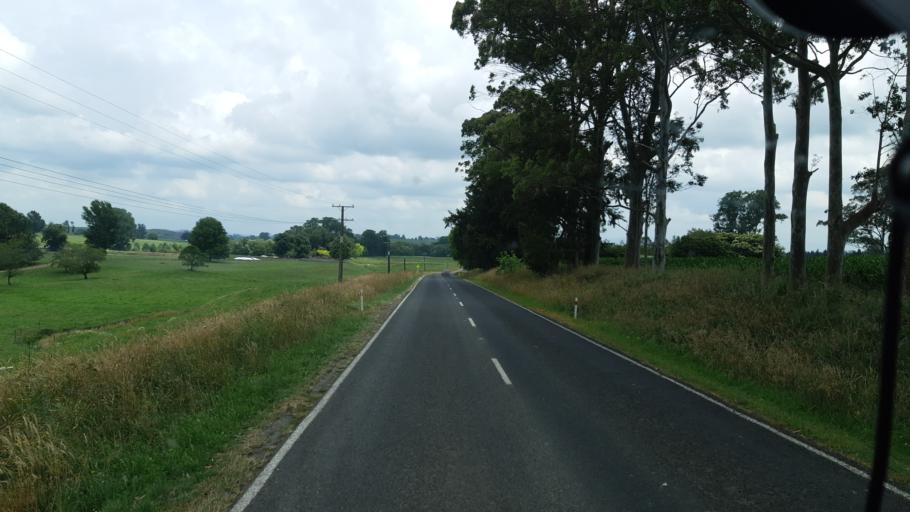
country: NZ
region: Waikato
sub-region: Waipa District
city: Cambridge
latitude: -38.1029
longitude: 175.4470
